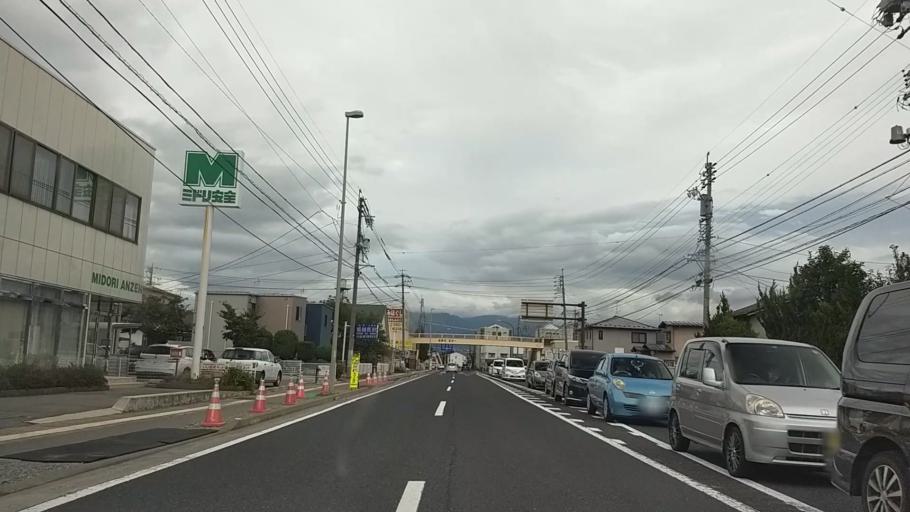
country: JP
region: Nagano
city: Nagano-shi
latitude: 36.6477
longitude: 138.2164
